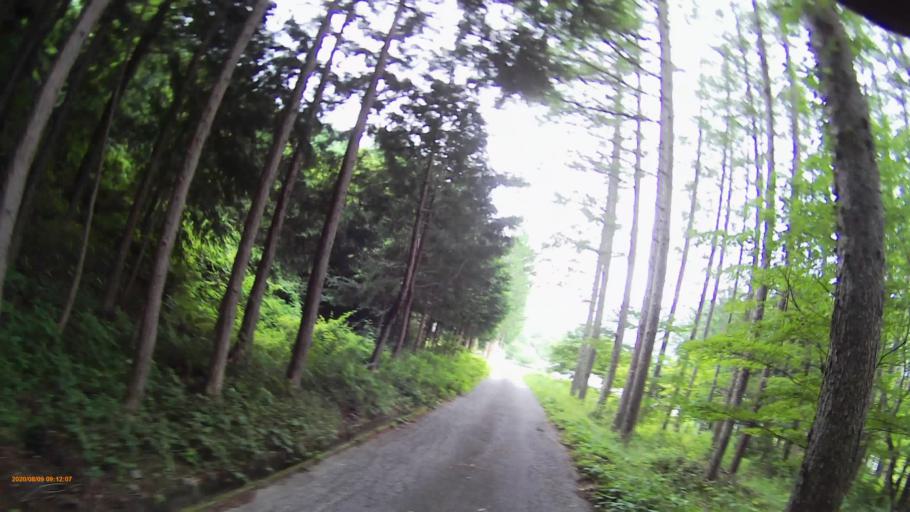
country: JP
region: Nagano
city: Ina
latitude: 35.9452
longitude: 137.7880
